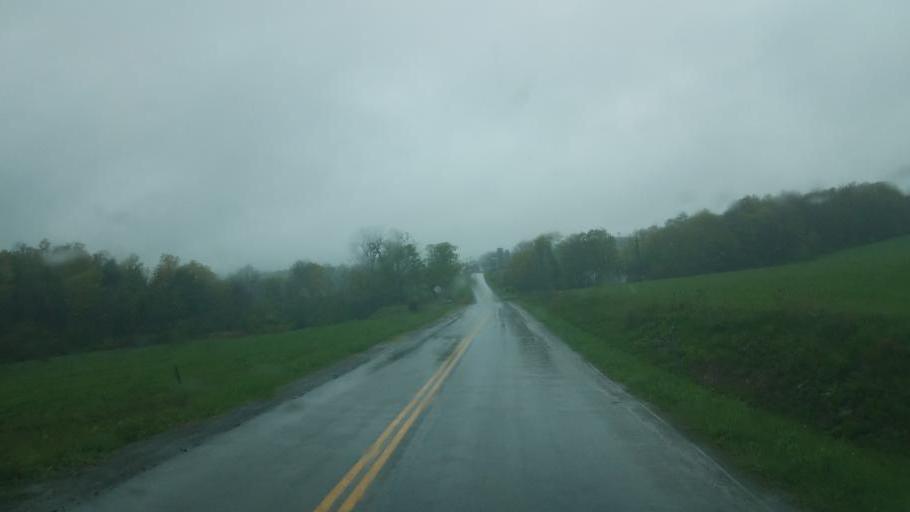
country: US
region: Pennsylvania
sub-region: Tioga County
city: Westfield
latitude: 42.0817
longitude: -77.4867
